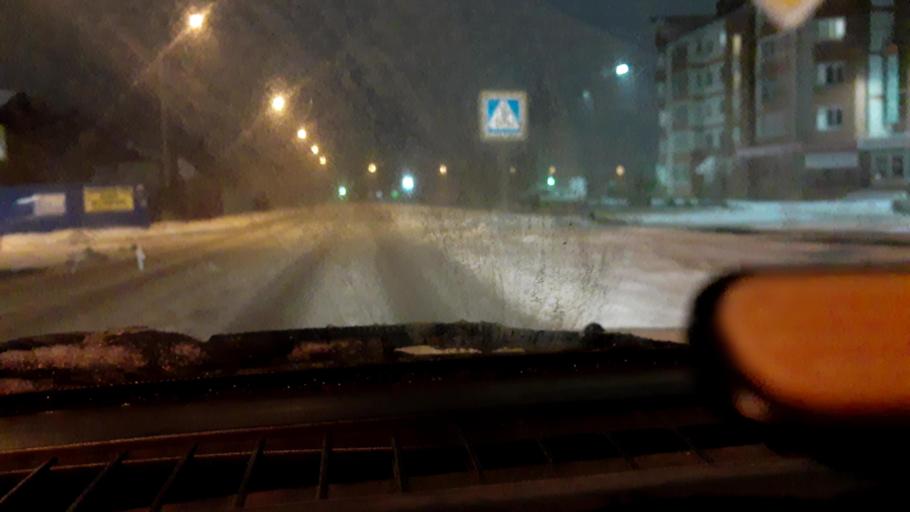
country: RU
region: Nizjnij Novgorod
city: Kstovo
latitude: 56.1407
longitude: 44.1920
